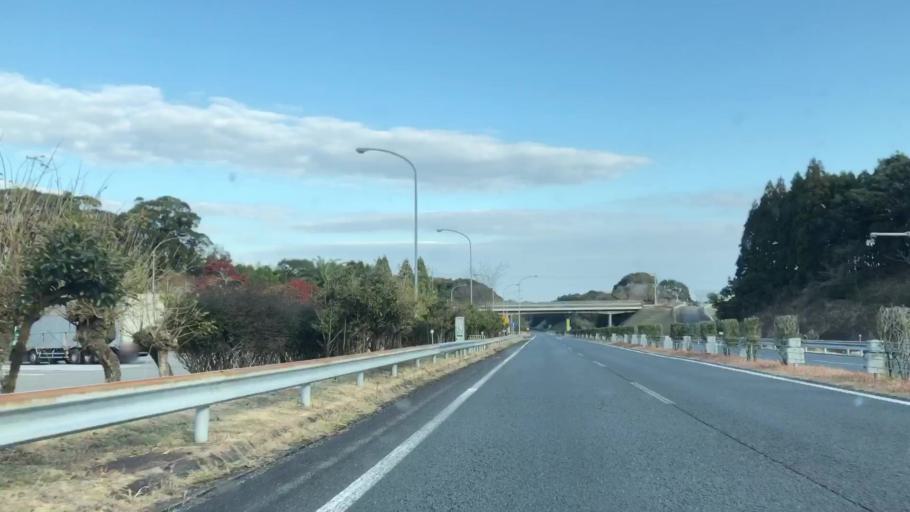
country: JP
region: Miyazaki
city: Miyazaki-shi
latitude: 31.8677
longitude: 131.4012
